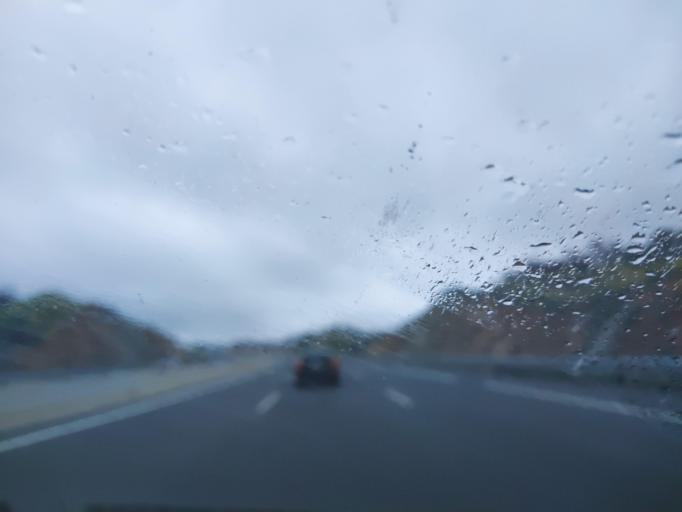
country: ES
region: Castille-La Mancha
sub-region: Province of Toledo
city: Guadamur
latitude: 39.8608
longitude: -4.0962
